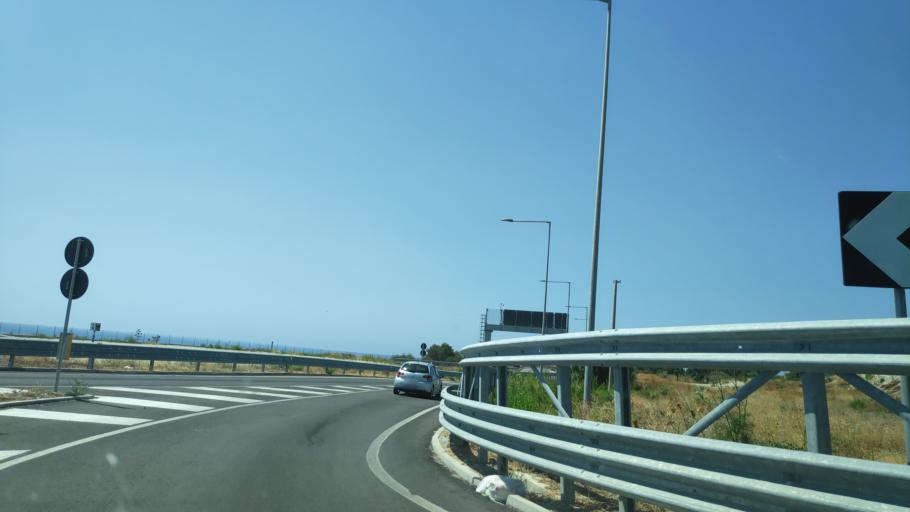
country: IT
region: Calabria
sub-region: Provincia di Reggio Calabria
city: Palizzi Marina
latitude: 37.9220
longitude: 16.0128
